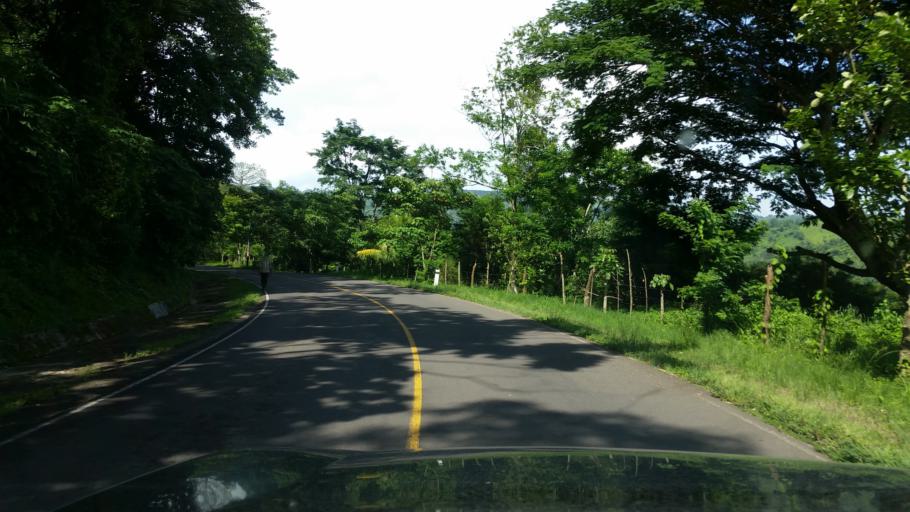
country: NI
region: Matagalpa
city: San Ramon
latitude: 13.0049
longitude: -85.8031
